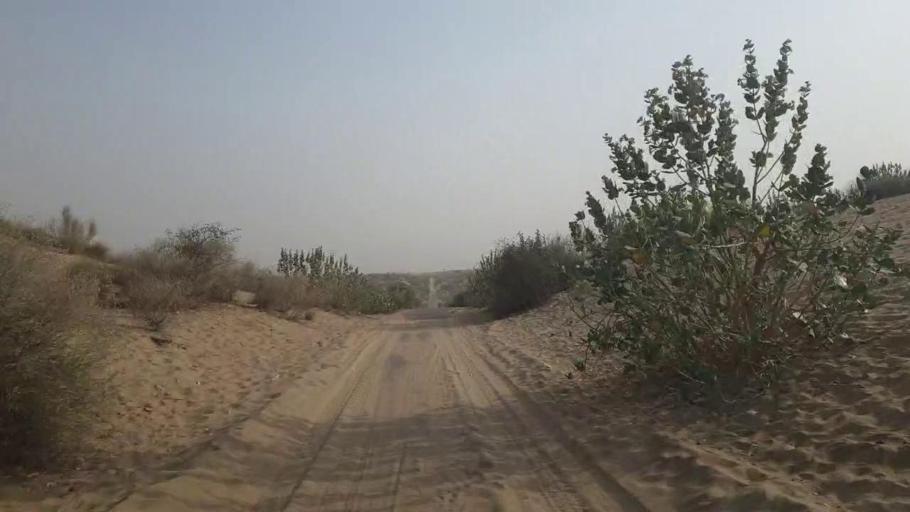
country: PK
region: Sindh
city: Chor
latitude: 25.4427
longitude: 69.9651
